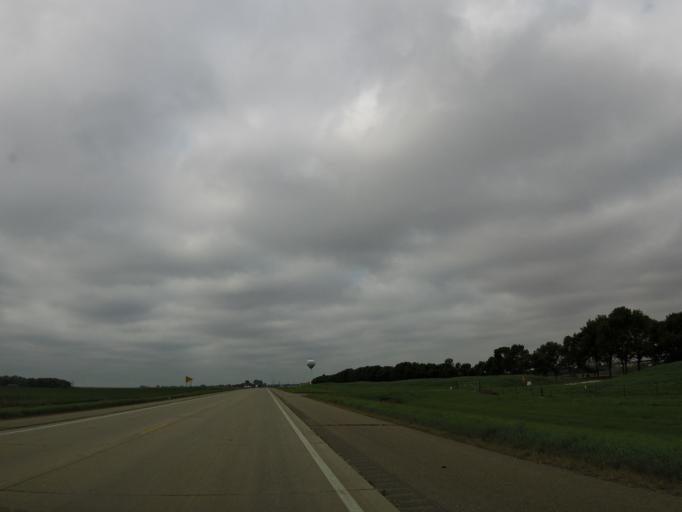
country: US
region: Minnesota
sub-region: Renville County
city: Renville
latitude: 44.7893
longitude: -95.1699
